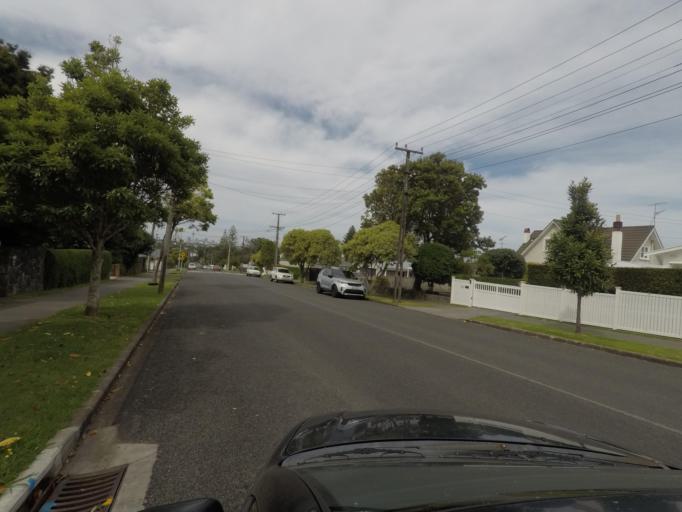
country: NZ
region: Auckland
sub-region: Auckland
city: Auckland
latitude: -36.8863
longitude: 174.7226
